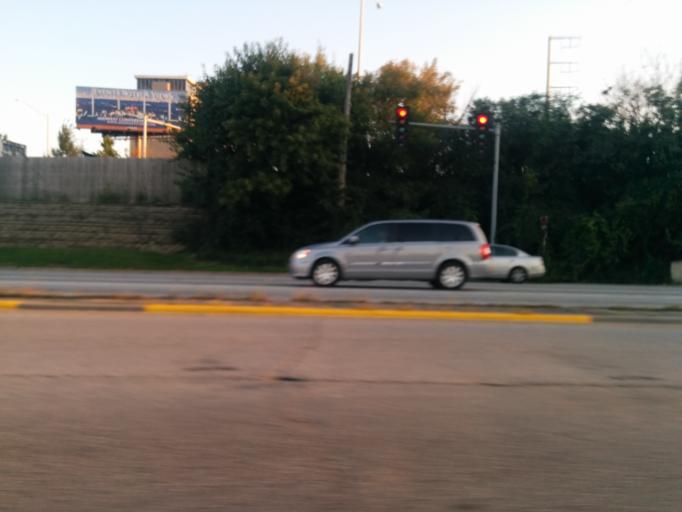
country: US
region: Illinois
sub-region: DuPage County
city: Elmhurst
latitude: 41.9070
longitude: -87.9186
